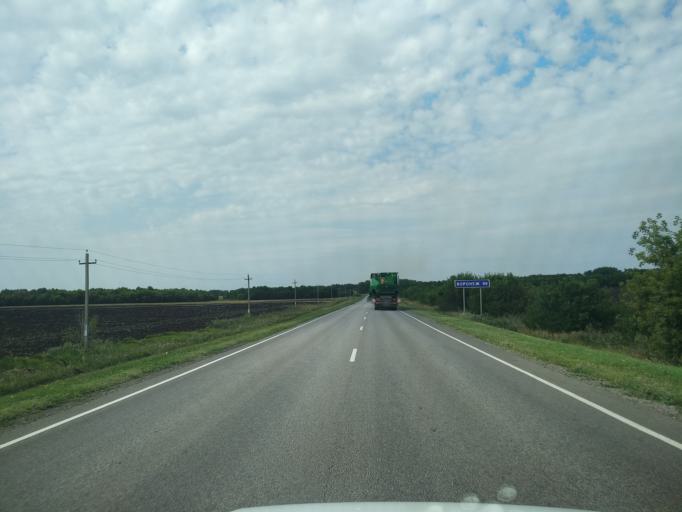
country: RU
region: Voronezj
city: Pereleshinskiy
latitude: 51.8815
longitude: 40.4208
